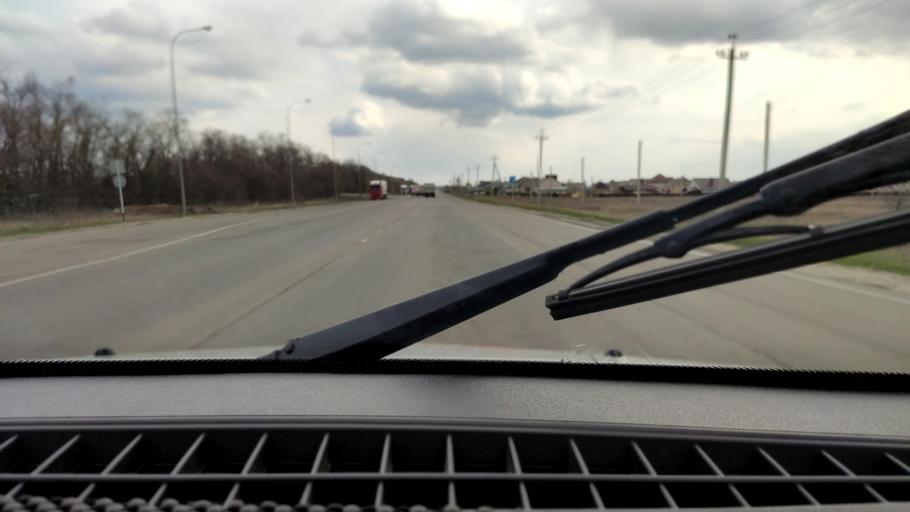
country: RU
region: Voronezj
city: Novaya Usman'
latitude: 51.6229
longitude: 39.3350
